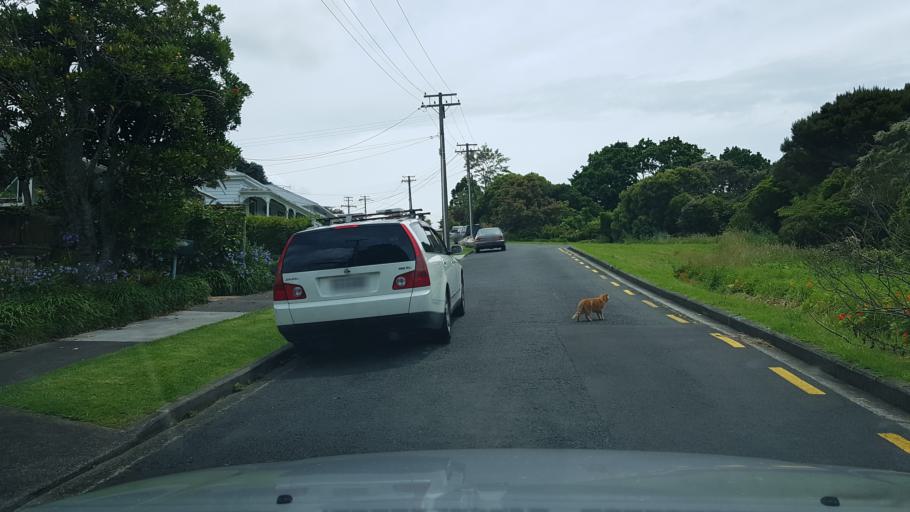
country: NZ
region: Auckland
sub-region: Auckland
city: North Shore
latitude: -36.8161
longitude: 174.7229
